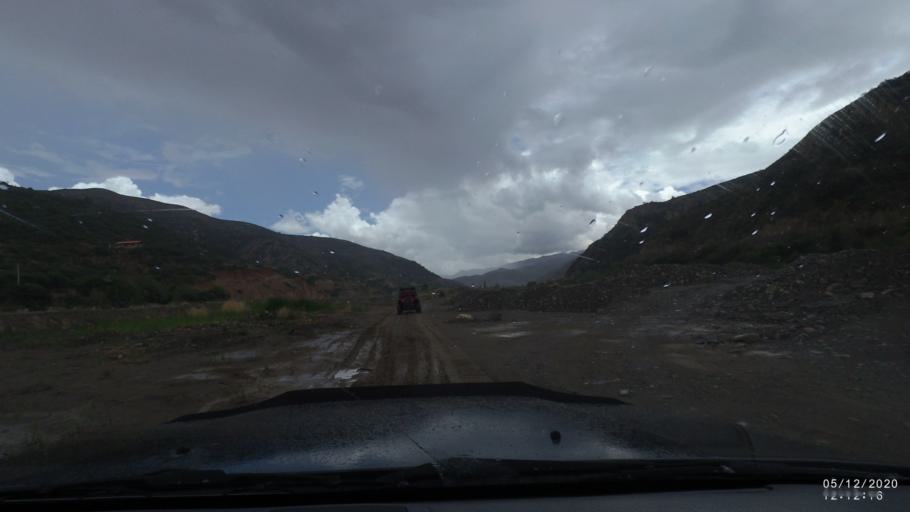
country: BO
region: Cochabamba
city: Sipe Sipe
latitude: -17.5640
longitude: -66.3754
